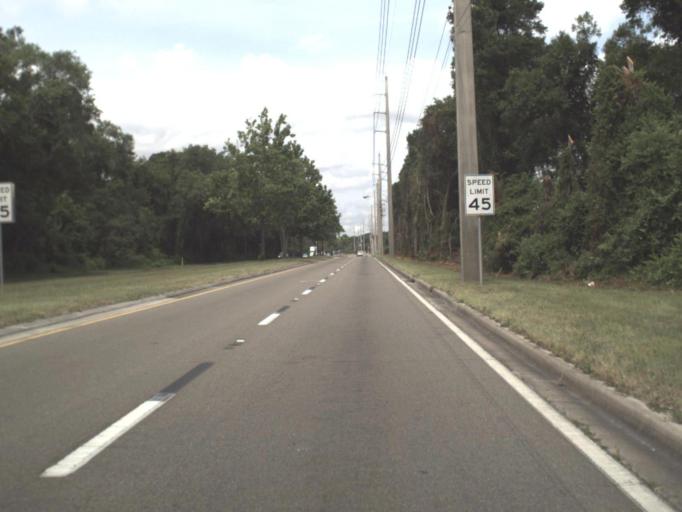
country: US
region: Florida
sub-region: Duval County
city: Jacksonville
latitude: 30.4076
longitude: -81.6316
